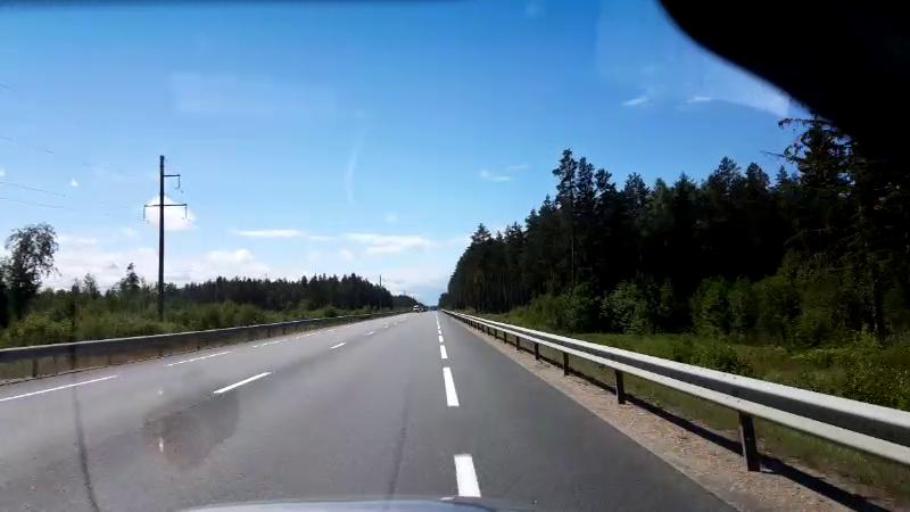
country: LV
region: Saulkrastu
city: Saulkrasti
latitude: 57.2184
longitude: 24.4045
